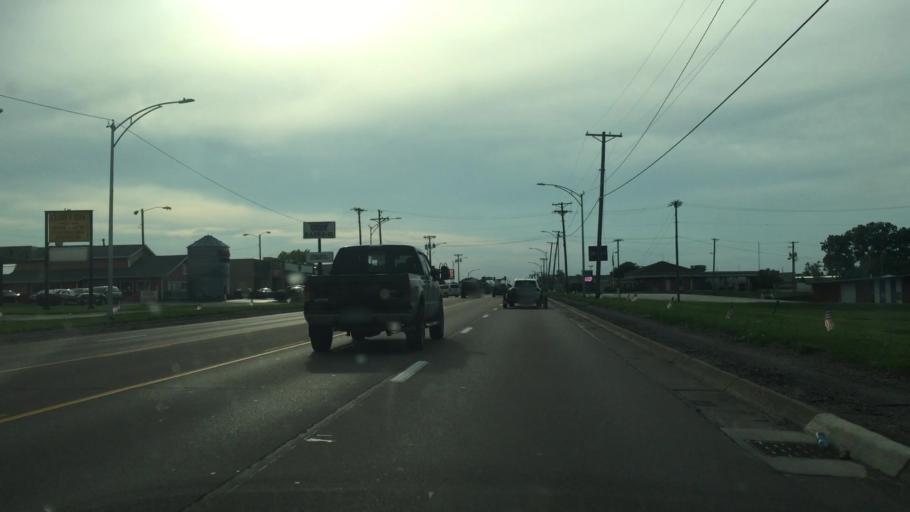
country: US
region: Missouri
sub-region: Pettis County
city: Sedalia
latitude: 38.7073
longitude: -93.2616
